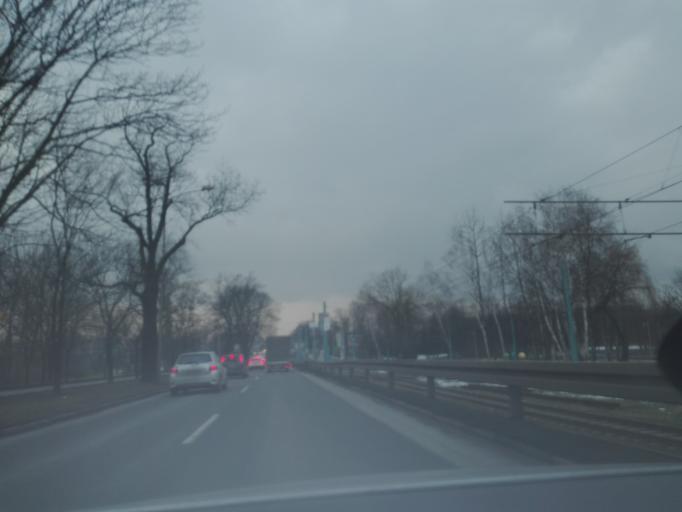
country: PL
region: Silesian Voivodeship
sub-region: Chorzow
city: Chorzow
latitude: 50.2861
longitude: 18.9699
